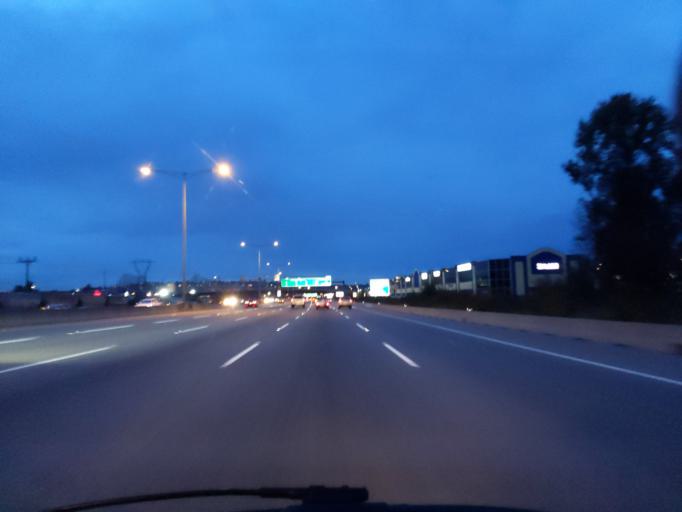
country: CA
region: British Columbia
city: Port Moody
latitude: 49.2318
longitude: -122.8555
